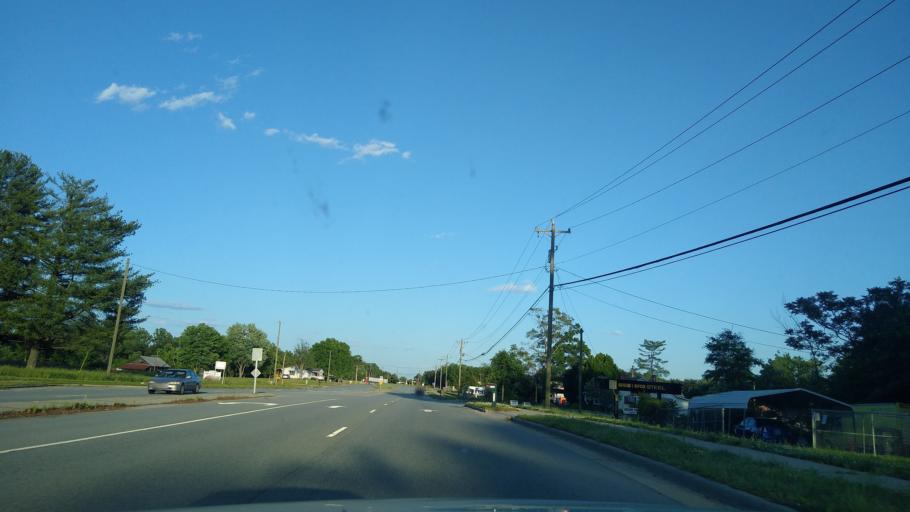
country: US
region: North Carolina
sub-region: Guilford County
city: Oak Ridge
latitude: 36.1038
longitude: -80.0020
